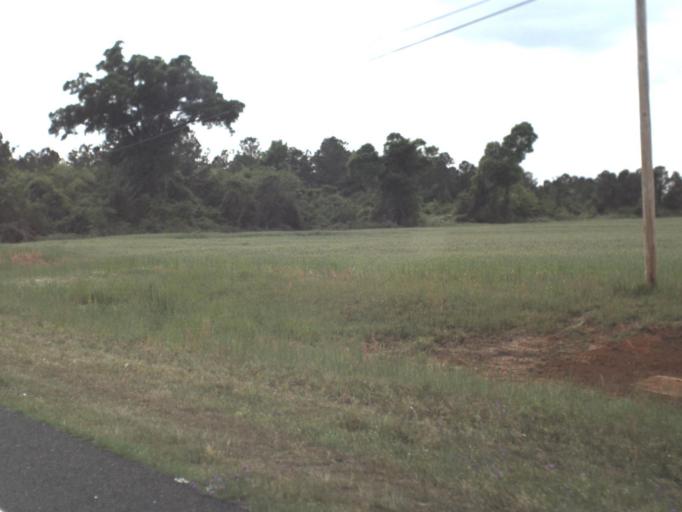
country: US
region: Florida
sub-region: Escambia County
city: Century
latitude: 30.9279
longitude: -87.3052
